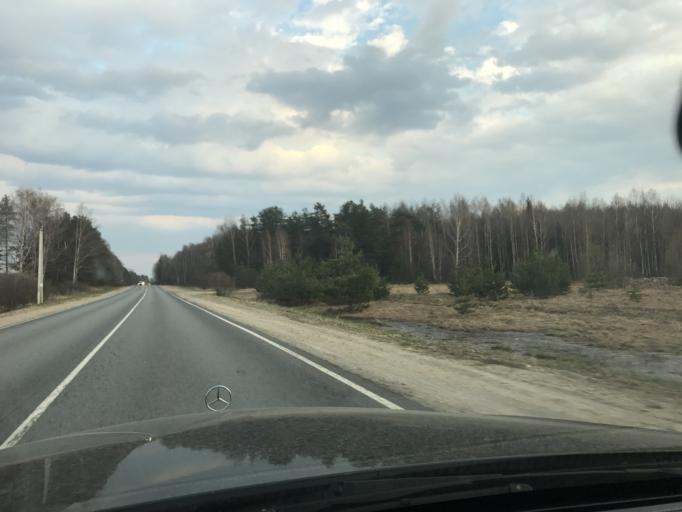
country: RU
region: Vladimir
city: Murom
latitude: 55.6375
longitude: 41.8595
